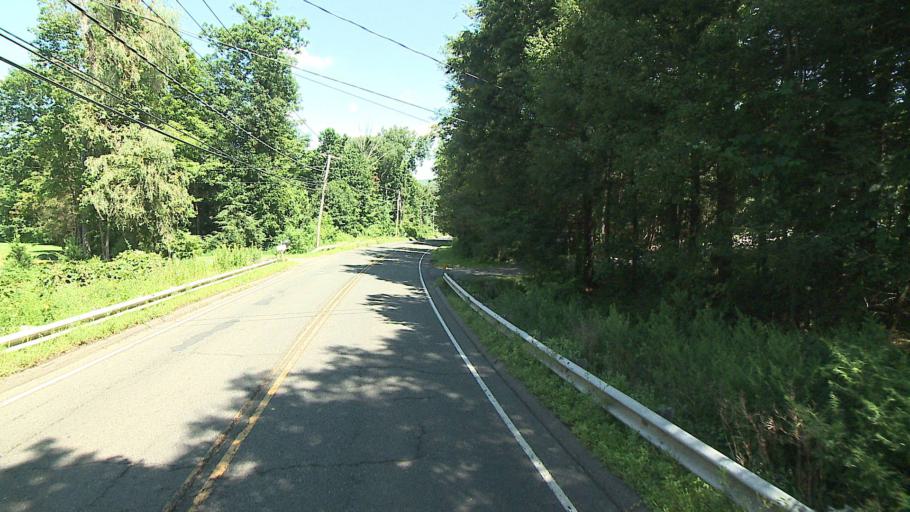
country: US
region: Connecticut
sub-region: New Haven County
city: Oxford
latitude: 41.3801
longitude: -73.1925
